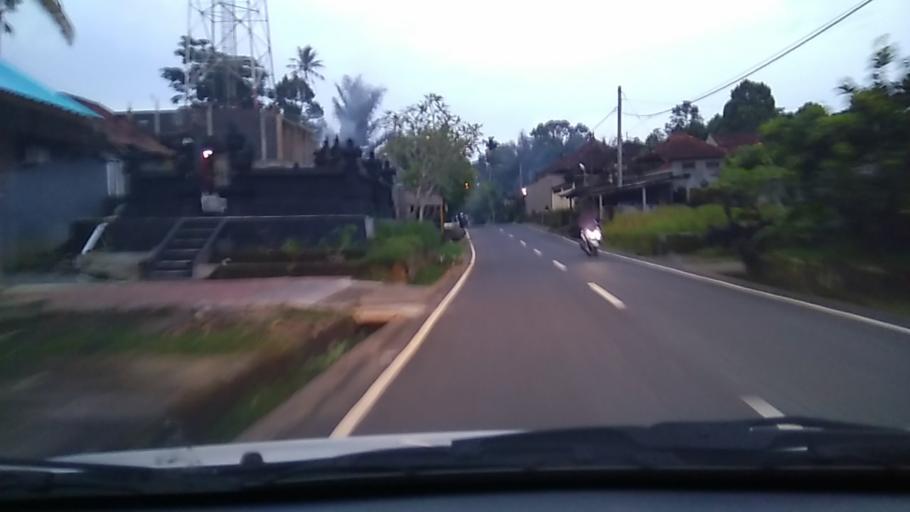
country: ID
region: Bali
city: Basa
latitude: -8.4737
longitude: 115.1840
